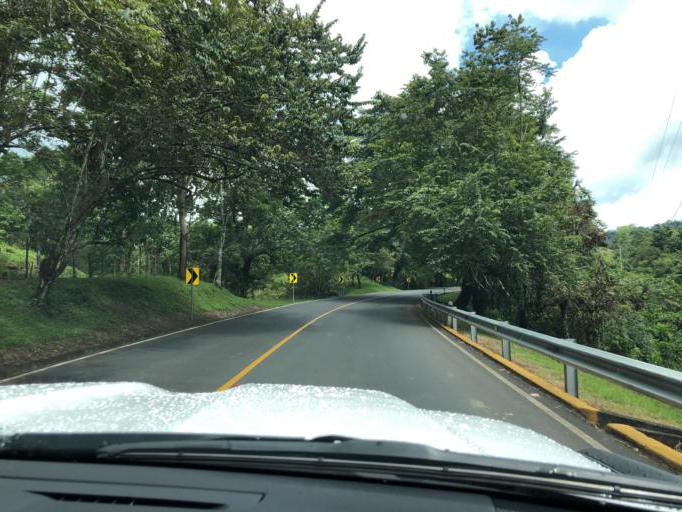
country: NI
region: Chontales
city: Villa Sandino
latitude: 11.9948
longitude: -84.9111
